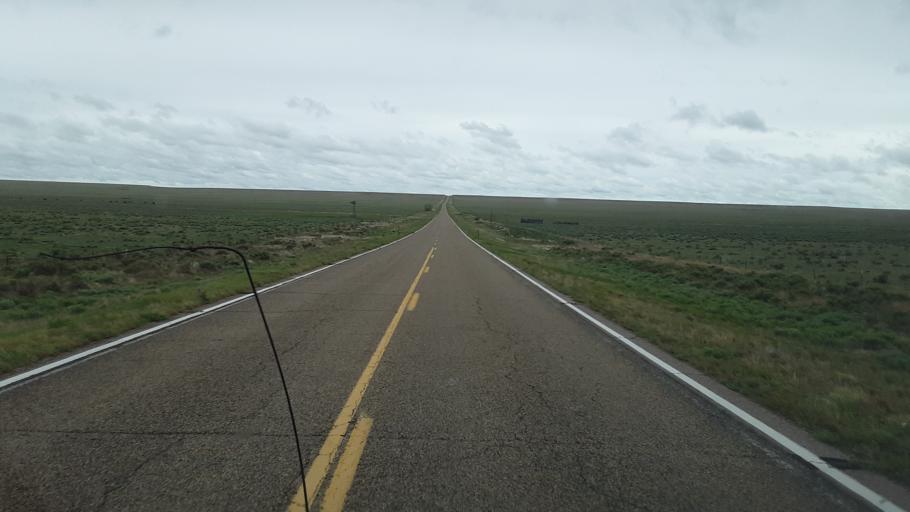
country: US
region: Colorado
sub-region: Lincoln County
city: Hugo
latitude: 38.8498
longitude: -103.3621
